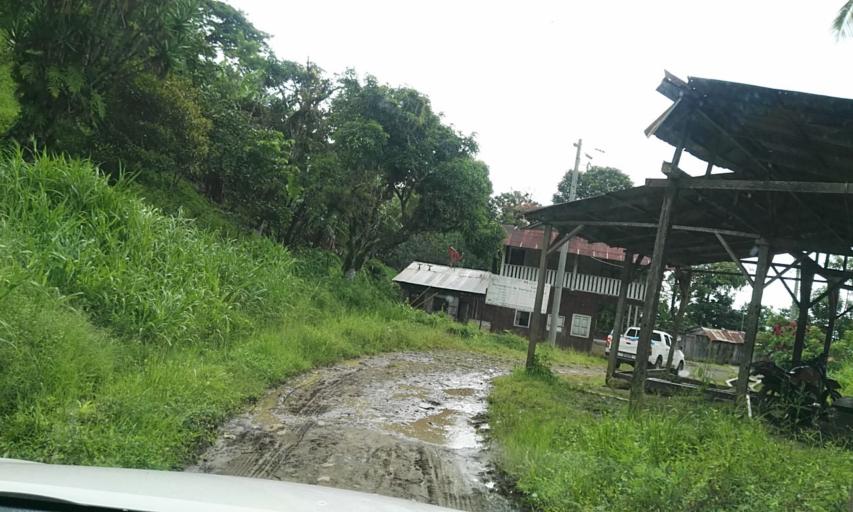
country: NI
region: Matagalpa
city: Matagalpa
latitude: 13.0187
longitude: -85.8794
